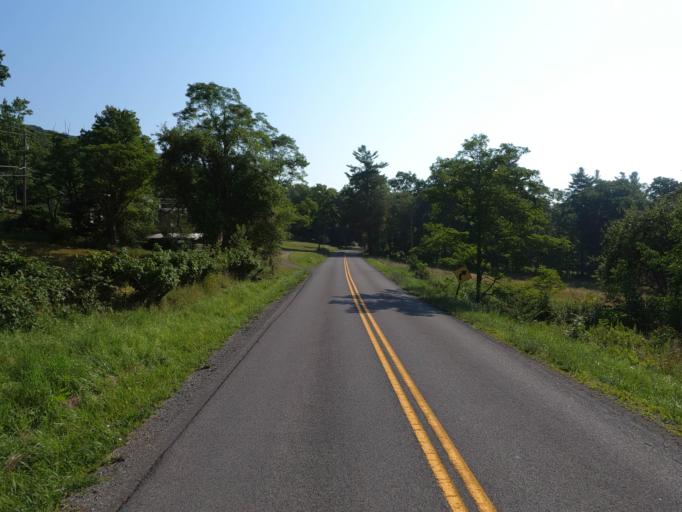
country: US
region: Maryland
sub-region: Garrett County
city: Mountain Lake Park
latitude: 39.4955
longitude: -79.3534
